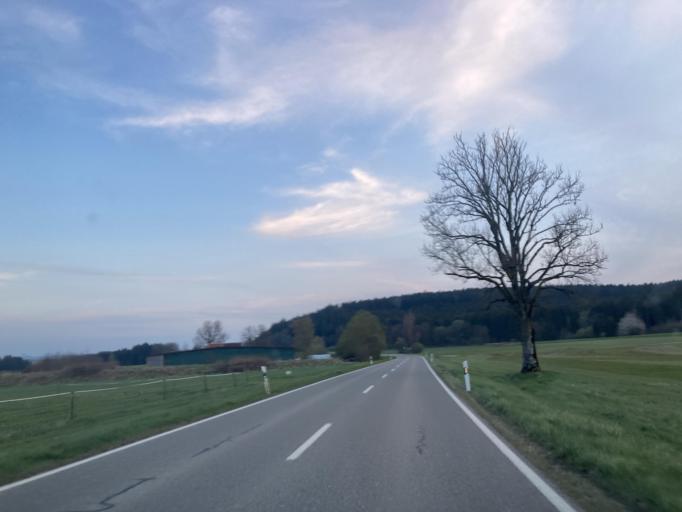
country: DE
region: Baden-Wuerttemberg
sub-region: Freiburg Region
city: Wellendingen
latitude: 48.1712
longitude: 8.7201
